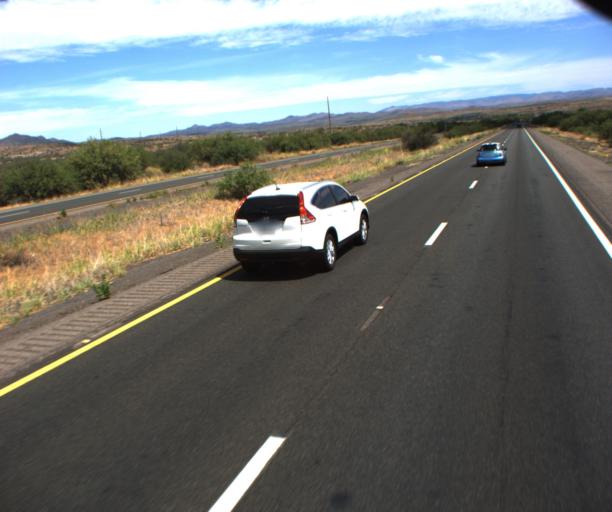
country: US
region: Arizona
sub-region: Yavapai County
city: Spring Valley
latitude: 34.3551
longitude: -112.1171
